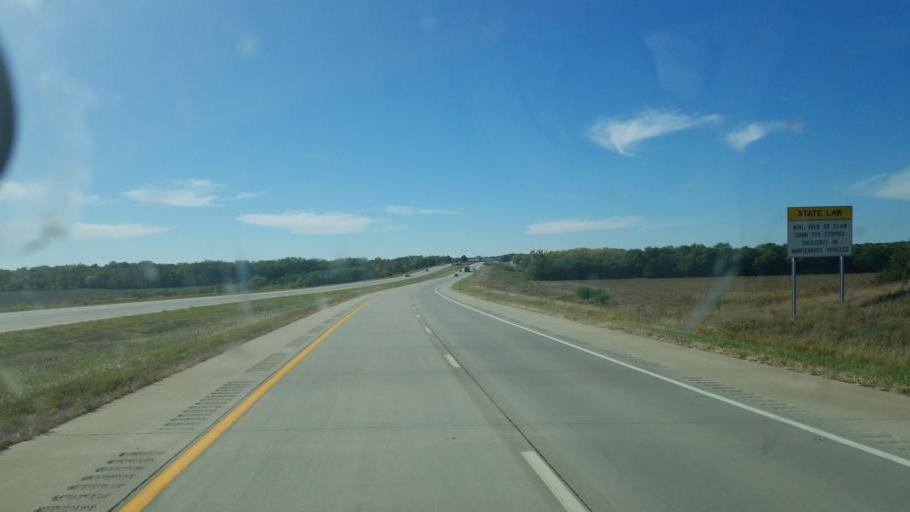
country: US
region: Kansas
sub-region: Dickinson County
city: Abilene
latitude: 38.9386
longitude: -97.2231
